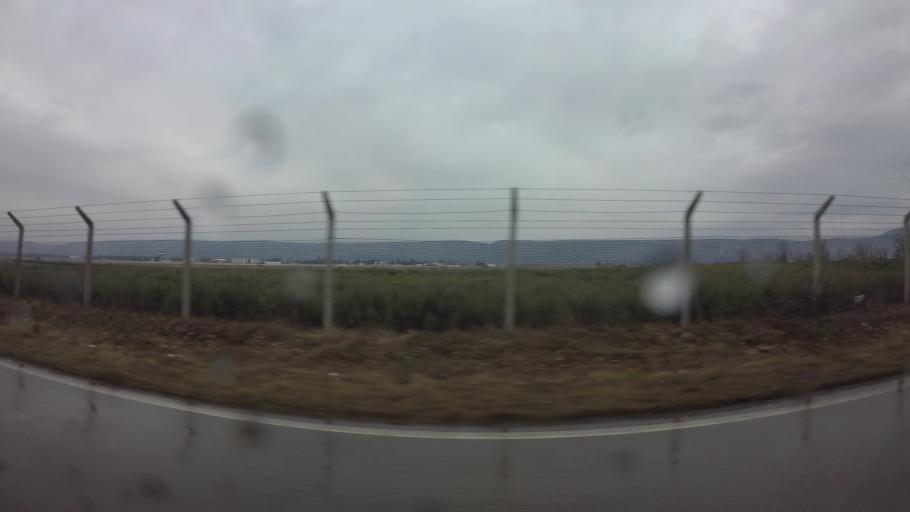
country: BA
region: Federation of Bosnia and Herzegovina
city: Rodoc
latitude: 43.2941
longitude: 17.8446
